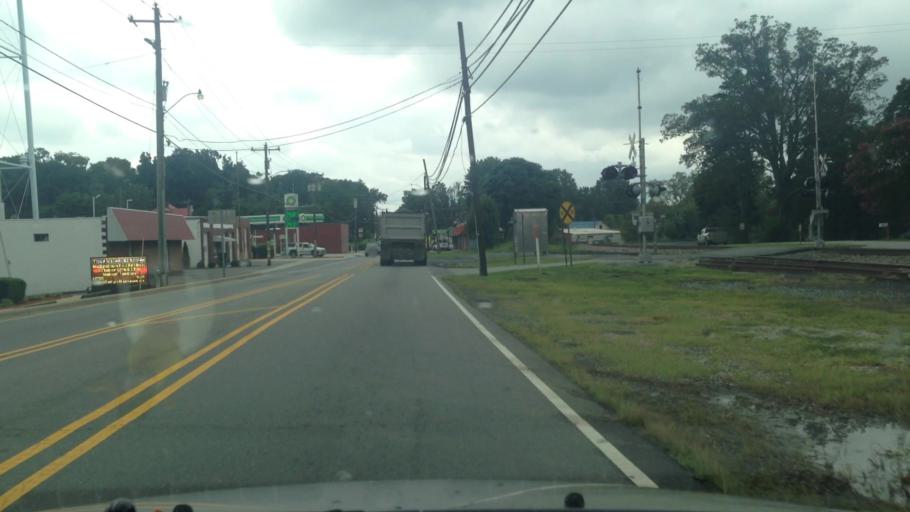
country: US
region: North Carolina
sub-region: Forsyth County
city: Walkertown
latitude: 36.1774
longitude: -80.1529
